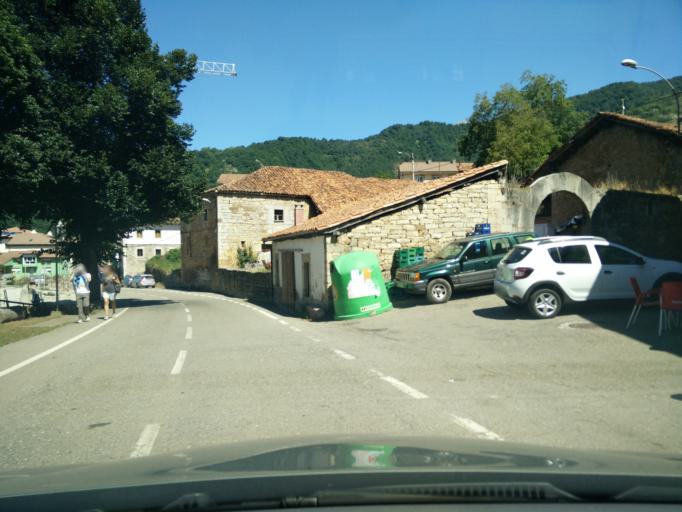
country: ES
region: Castille and Leon
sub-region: Provincia de Leon
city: Oseja de Sajambre
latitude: 43.1358
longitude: -5.0375
